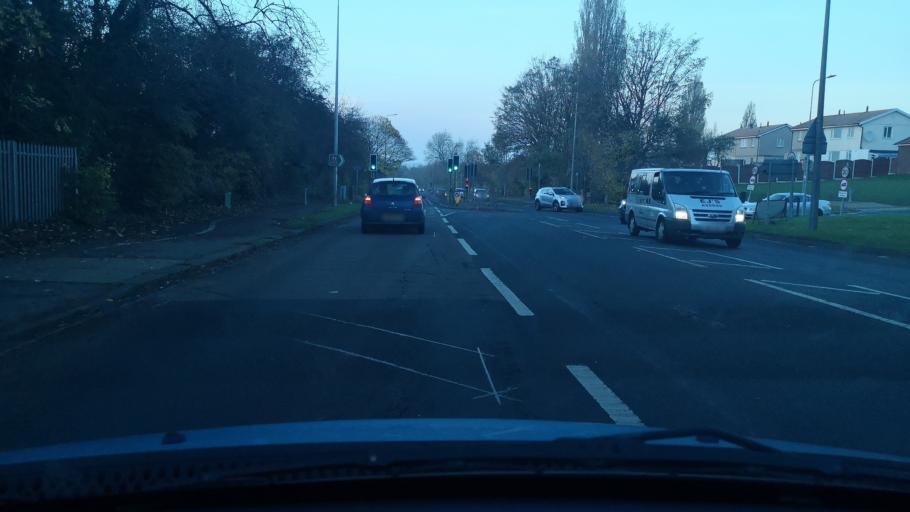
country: GB
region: England
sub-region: North Lincolnshire
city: Scunthorpe
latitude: 53.5851
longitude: -0.6732
